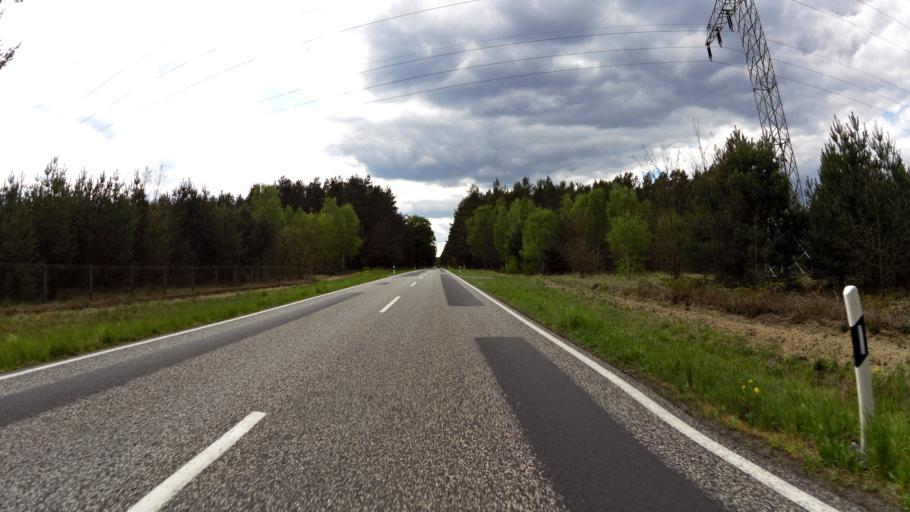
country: DE
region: Brandenburg
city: Spreenhagen
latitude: 52.3233
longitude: 13.9201
